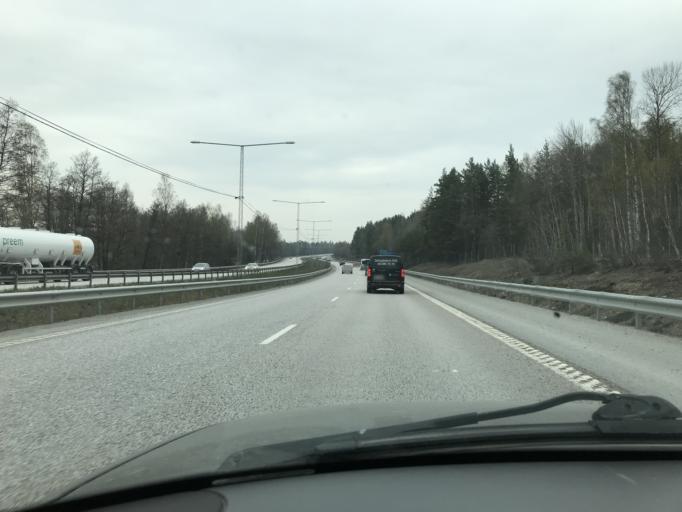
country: SE
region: Stockholm
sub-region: Vallentuna Kommun
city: Vallentuna
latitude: 59.4873
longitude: 18.1656
